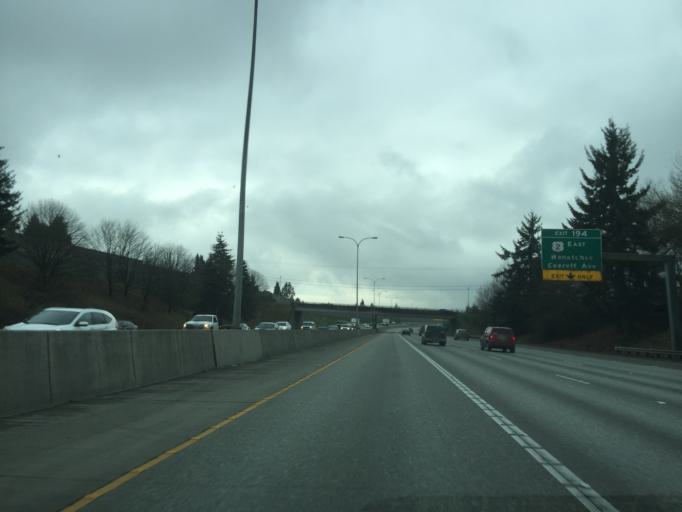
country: US
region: Washington
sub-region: Snohomish County
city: Everett
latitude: 47.9888
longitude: -122.1831
